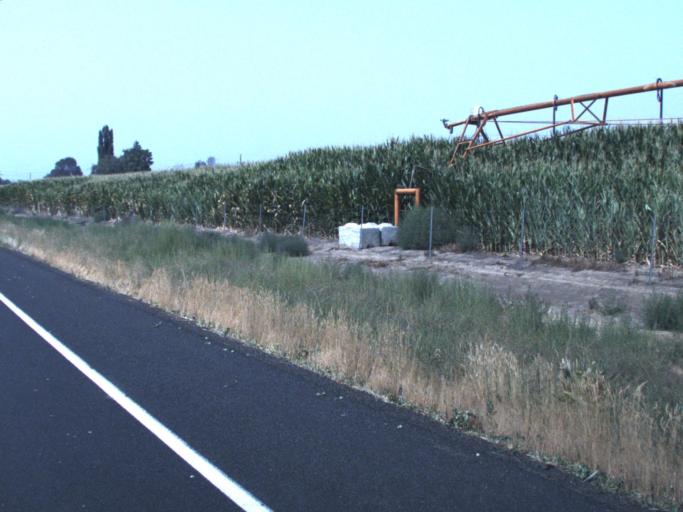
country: US
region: Washington
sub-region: Yakima County
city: Zillah
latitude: 46.5334
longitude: -120.2862
